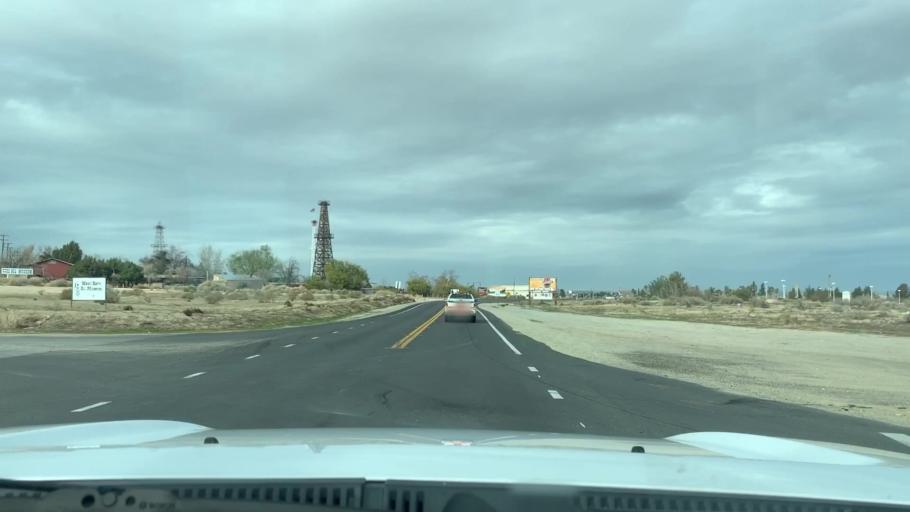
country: US
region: California
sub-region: Kern County
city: South Taft
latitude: 35.1317
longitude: -119.4456
